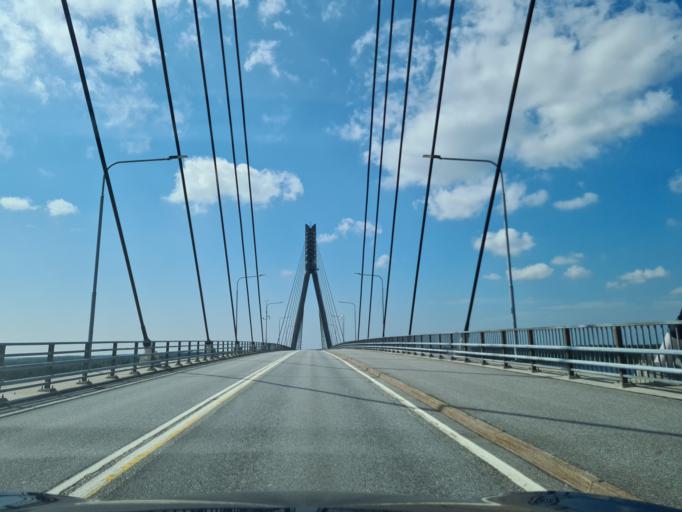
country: FI
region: Ostrobothnia
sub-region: Vaasa
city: Replot
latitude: 63.2066
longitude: 21.4752
